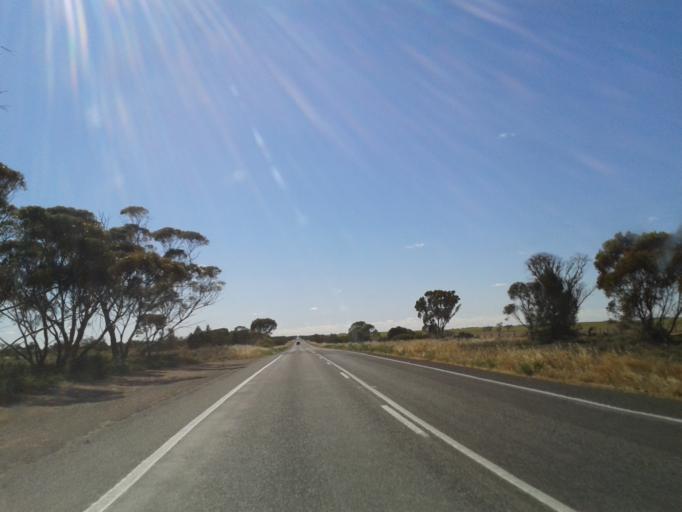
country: AU
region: South Australia
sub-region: Renmark Paringa
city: Renmark
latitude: -34.2744
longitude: 141.1969
